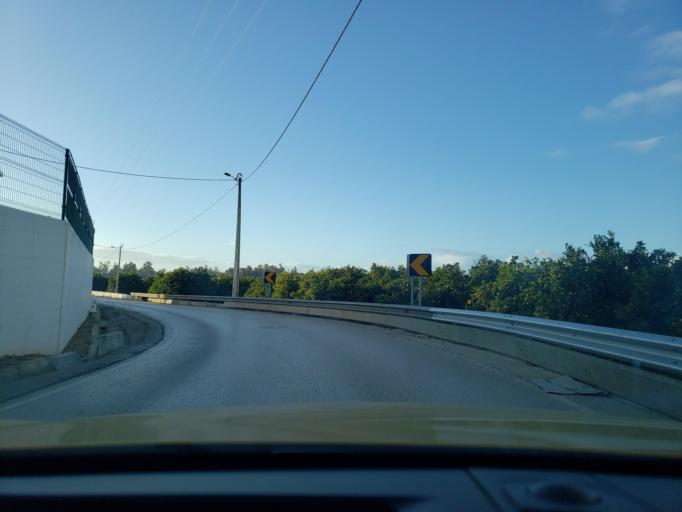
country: PT
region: Faro
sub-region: Portimao
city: Alvor
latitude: 37.1700
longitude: -8.5797
